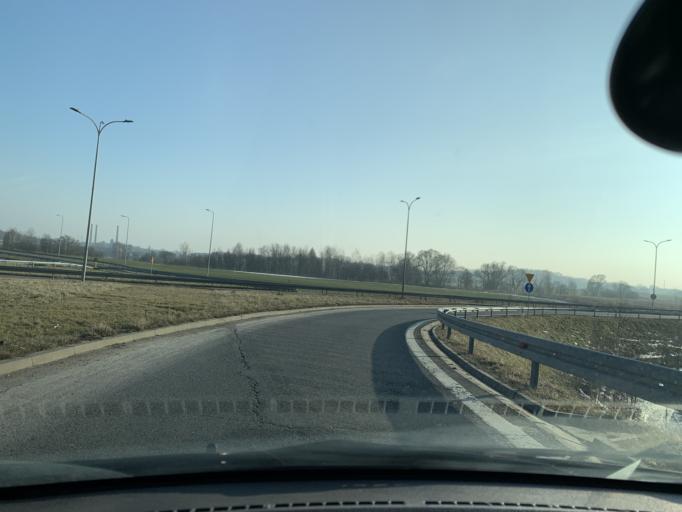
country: PL
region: Silesian Voivodeship
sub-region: Powiat tarnogorski
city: Radzionkow
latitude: 50.3674
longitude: 18.8738
